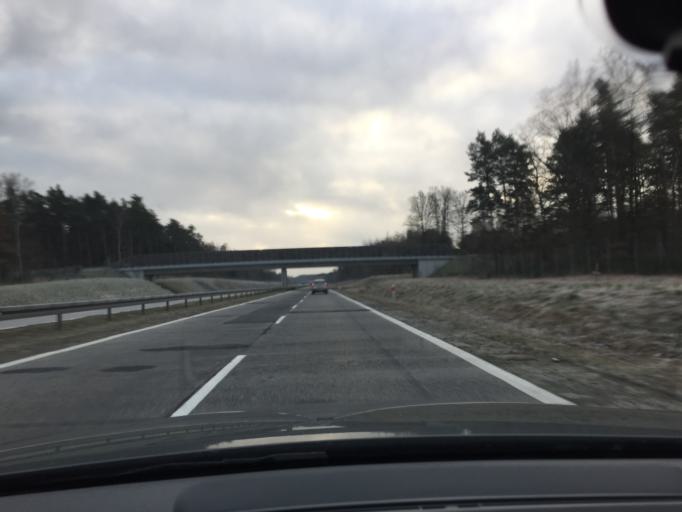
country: PL
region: Lubusz
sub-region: Powiat zarski
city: Lipinki Luzyckie
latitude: 51.5772
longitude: 15.0292
